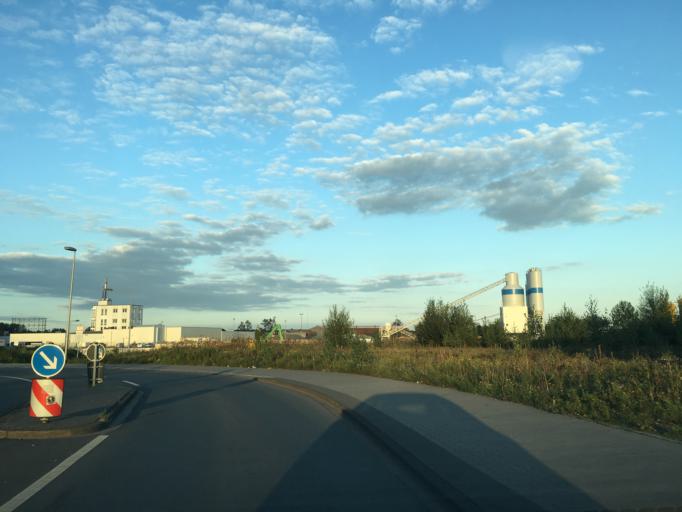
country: DE
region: North Rhine-Westphalia
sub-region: Regierungsbezirk Munster
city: Muenster
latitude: 51.9361
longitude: 7.6359
